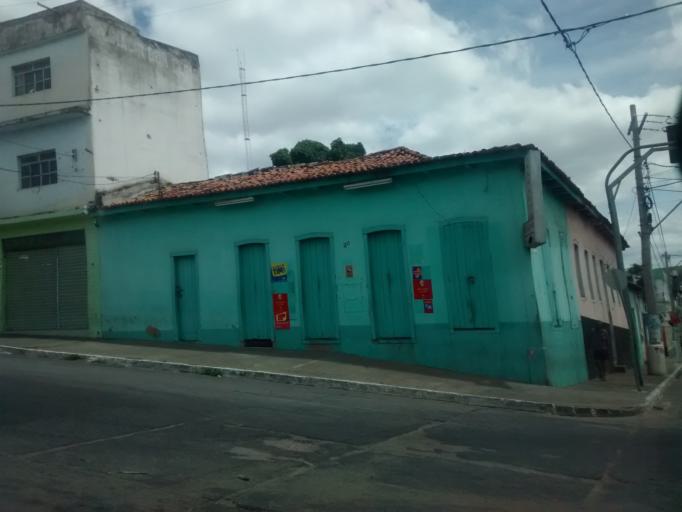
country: BR
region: Bahia
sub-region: Brumado
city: Brumado
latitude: -14.2030
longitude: -41.6638
